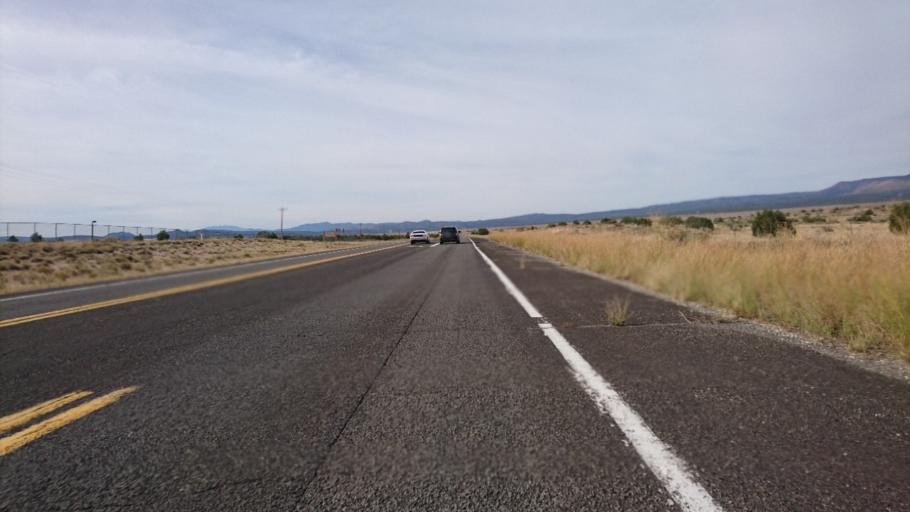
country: US
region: Arizona
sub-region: Mohave County
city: Peach Springs
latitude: 35.5023
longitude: -113.5273
